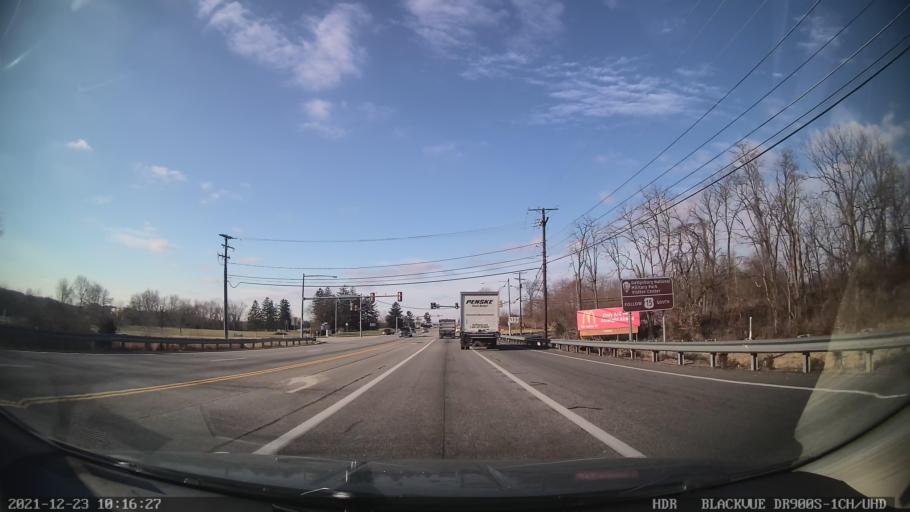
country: US
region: Pennsylvania
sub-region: Adams County
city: Lake Heritage
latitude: 39.8475
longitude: -77.1875
